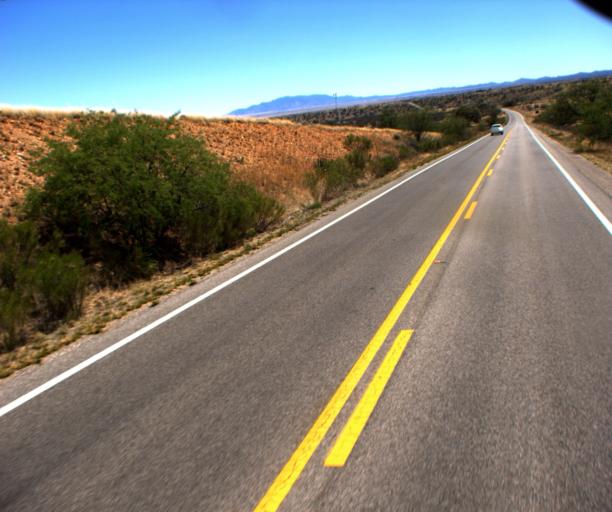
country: US
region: Arizona
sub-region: Pima County
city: Corona de Tucson
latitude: 31.7943
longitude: -110.7011
